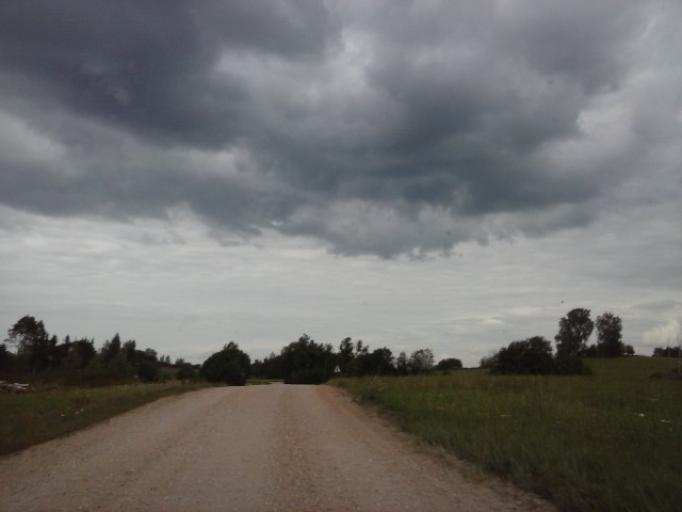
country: EE
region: Vorumaa
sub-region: Voru linn
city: Voru
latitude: 57.7471
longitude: 27.1364
